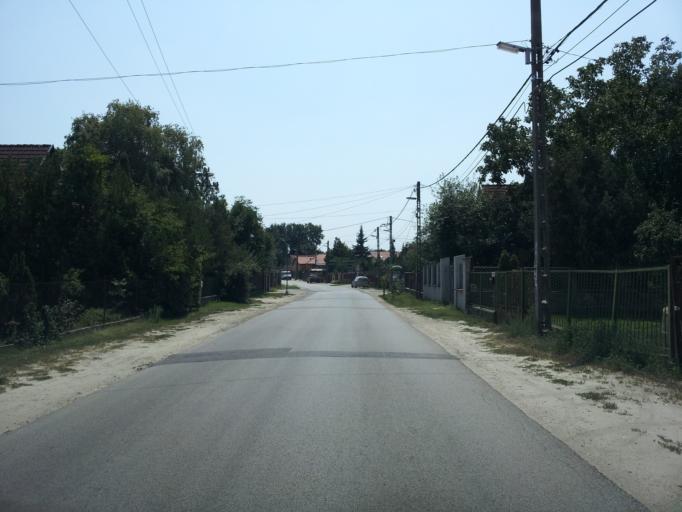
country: HU
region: Pest
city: Szigetszentmiklos
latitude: 47.3197
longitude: 19.0327
